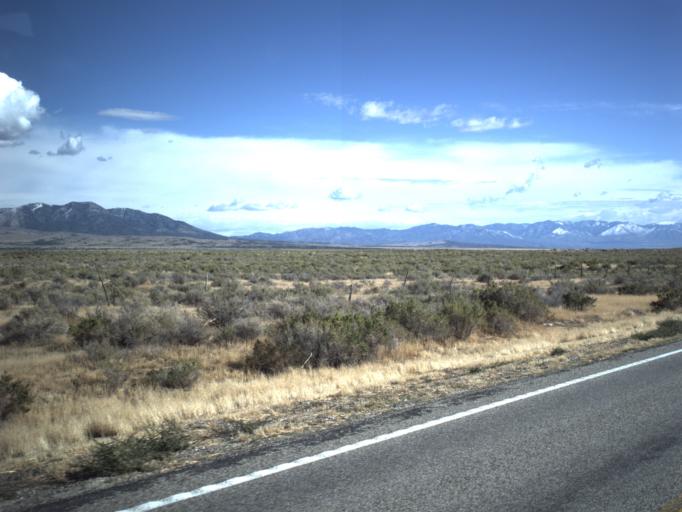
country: US
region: Utah
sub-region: Millard County
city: Delta
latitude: 39.3201
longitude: -112.4817
